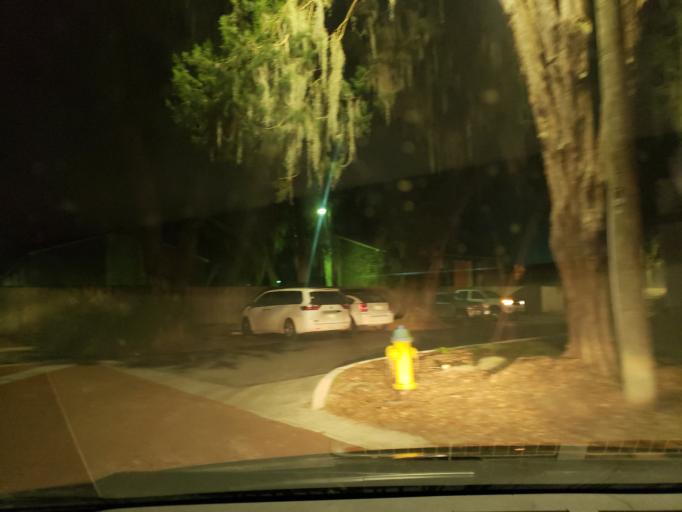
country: US
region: Georgia
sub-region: Chatham County
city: Montgomery
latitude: 31.9781
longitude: -81.1277
